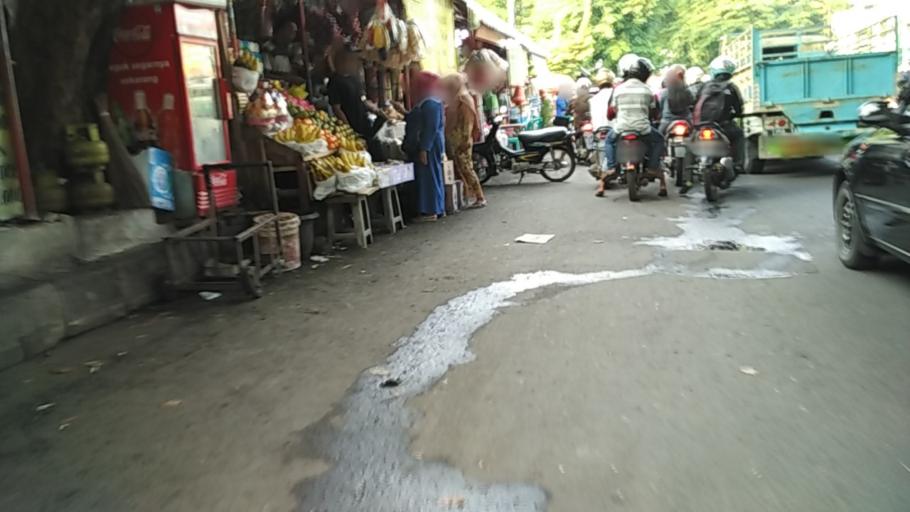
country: ID
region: Central Java
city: Semarang
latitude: -6.9949
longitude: 110.4104
